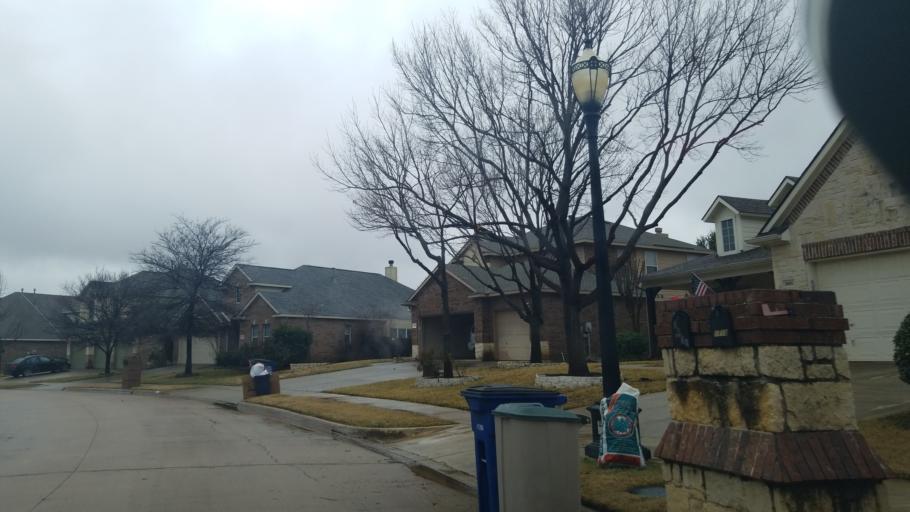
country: US
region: Texas
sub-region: Denton County
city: Corinth
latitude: 33.1524
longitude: -97.0819
